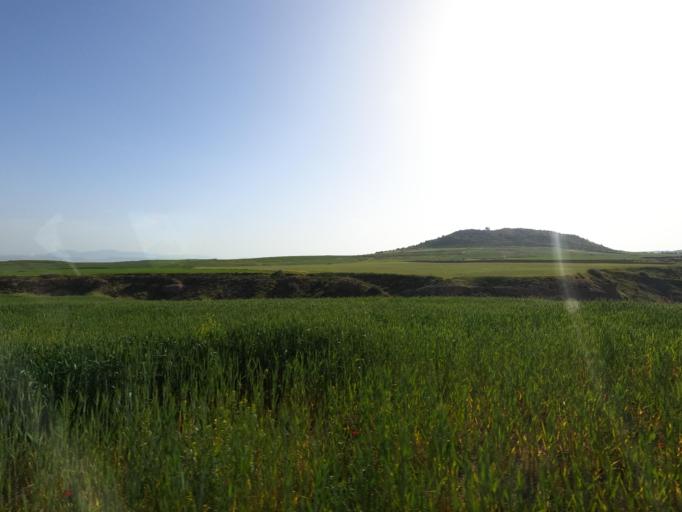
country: CY
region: Lefkosia
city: Lefka
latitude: 35.0933
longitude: 32.9441
